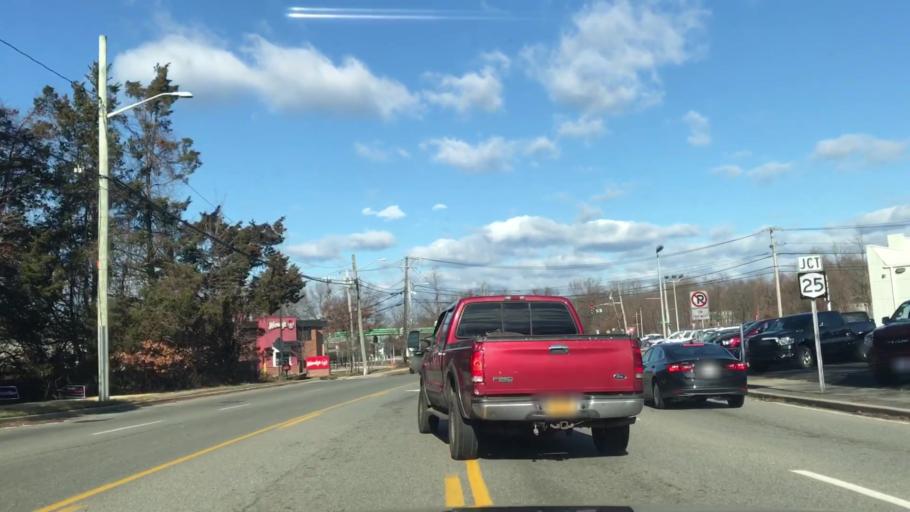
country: US
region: New York
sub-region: Suffolk County
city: Elwood
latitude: 40.8321
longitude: -73.3625
